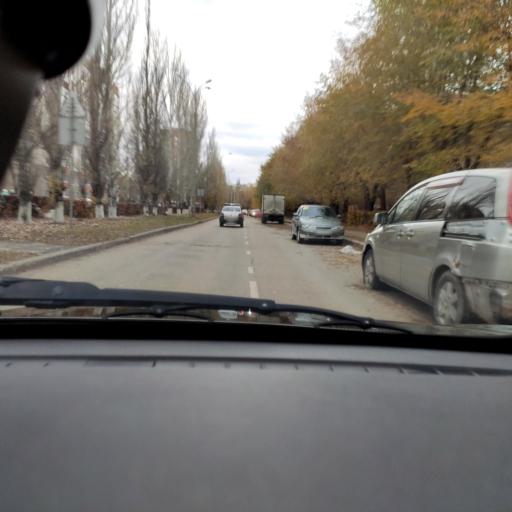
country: RU
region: Samara
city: Tol'yatti
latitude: 53.5309
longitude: 49.2923
